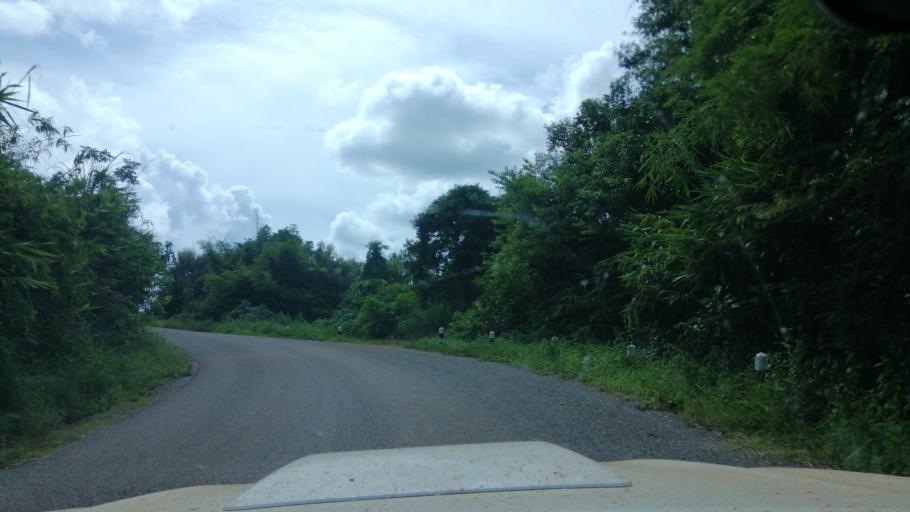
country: TH
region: Nan
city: Mae Charim
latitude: 18.3958
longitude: 101.1702
